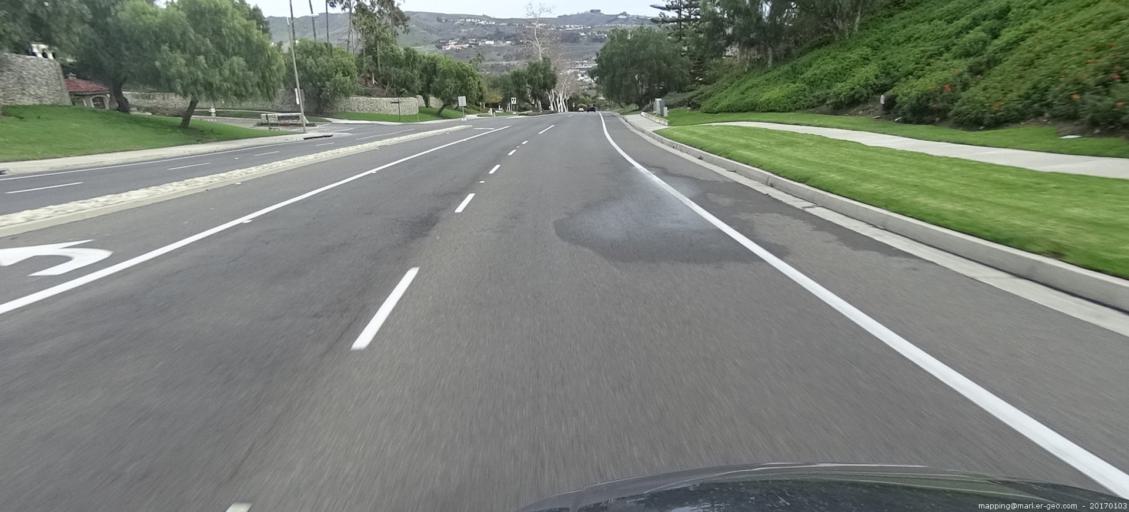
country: US
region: California
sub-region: Orange County
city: Dana Point
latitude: 33.4889
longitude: -117.6909
